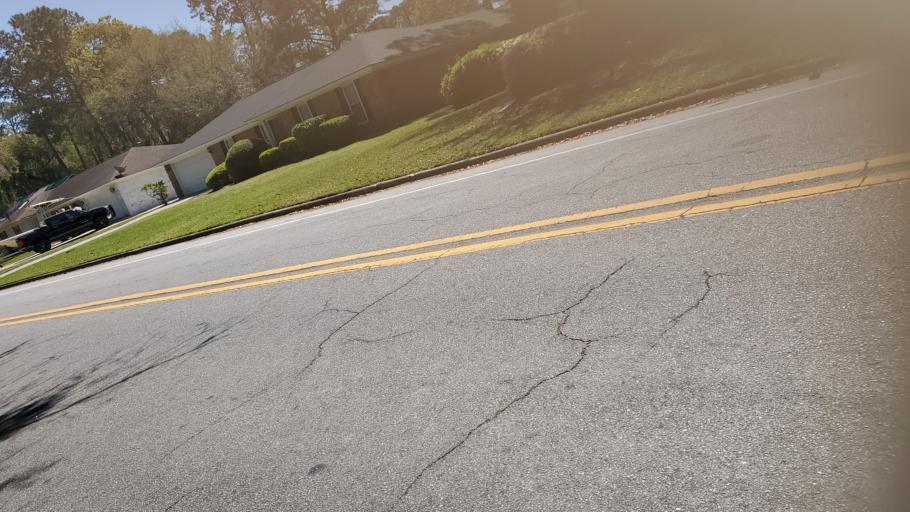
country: US
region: Georgia
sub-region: Chatham County
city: Wilmington Island
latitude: 32.0026
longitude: -80.9847
